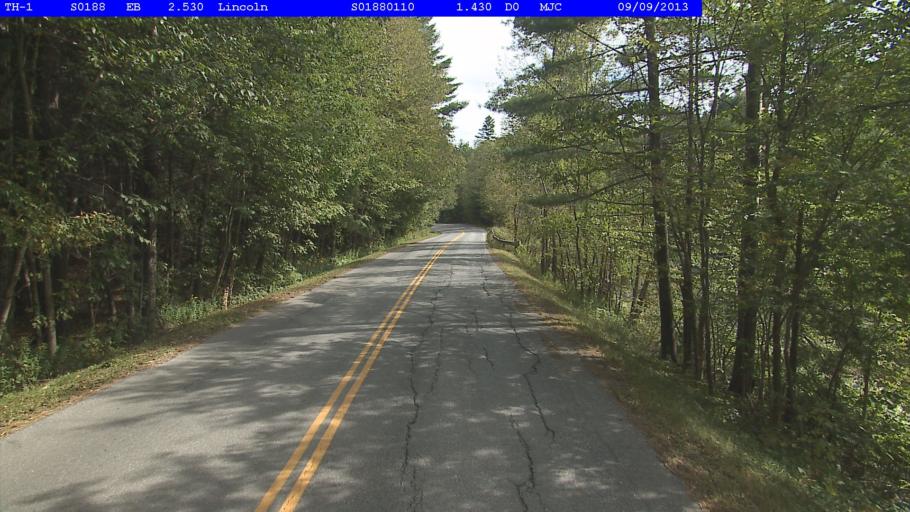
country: US
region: Vermont
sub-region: Addison County
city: Bristol
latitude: 44.1120
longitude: -73.0091
